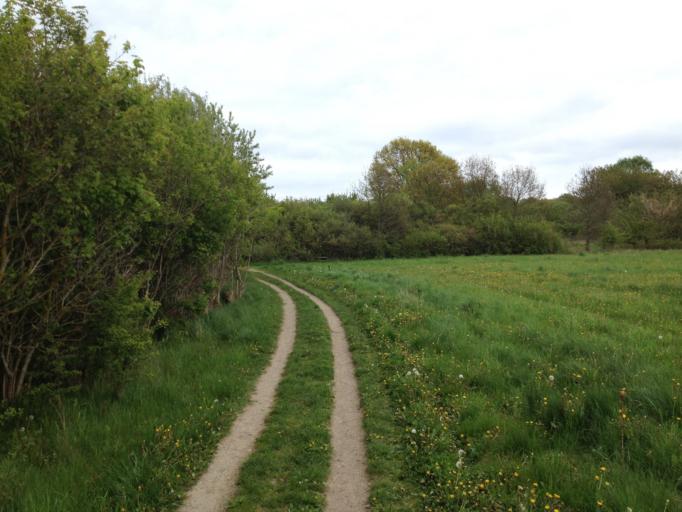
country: DK
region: Capital Region
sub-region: Fredensborg Kommune
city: Niva
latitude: 55.9486
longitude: 12.5067
